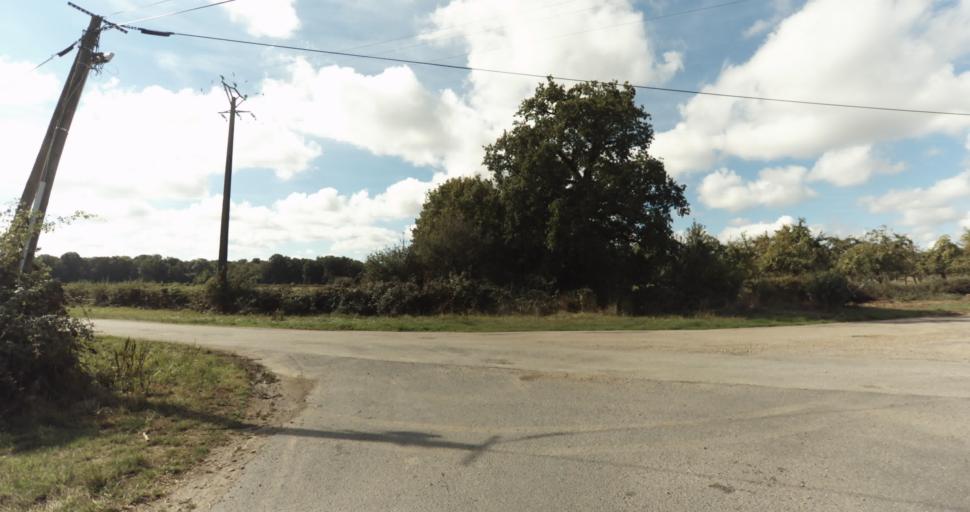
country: FR
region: Lower Normandy
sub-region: Departement du Calvados
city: La Vespiere
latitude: 48.9395
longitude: 0.3278
